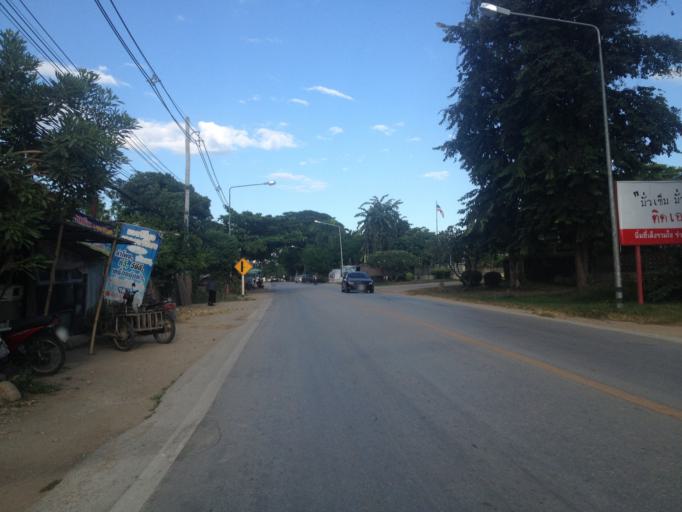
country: TH
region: Chiang Mai
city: San Pa Tong
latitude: 18.6129
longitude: 98.8545
